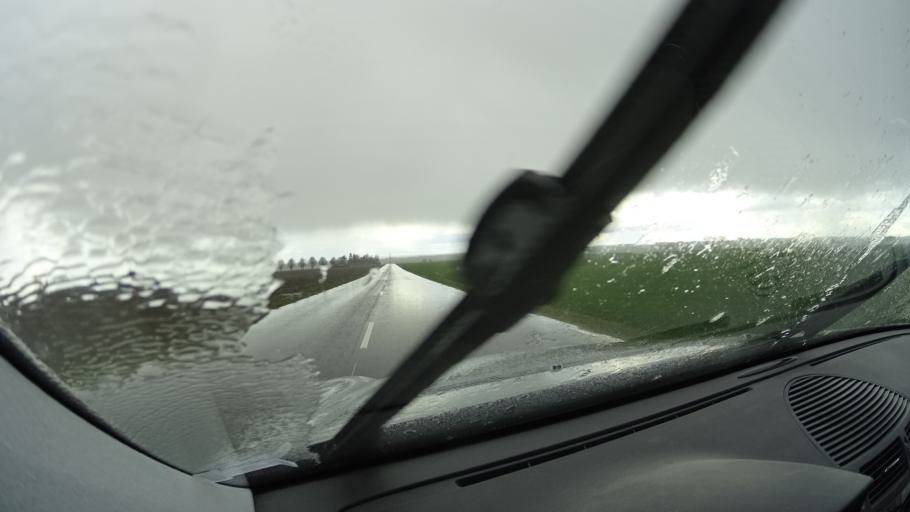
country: SE
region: Skane
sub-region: Lunds Kommun
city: Lund
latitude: 55.7620
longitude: 13.2233
